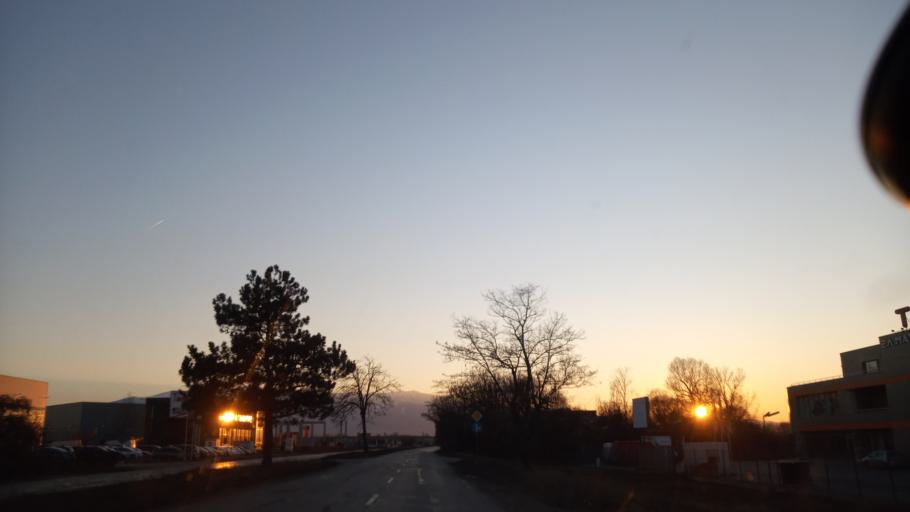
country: BG
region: Sofia-Capital
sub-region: Stolichna Obshtina
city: Sofia
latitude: 42.7163
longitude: 23.4388
